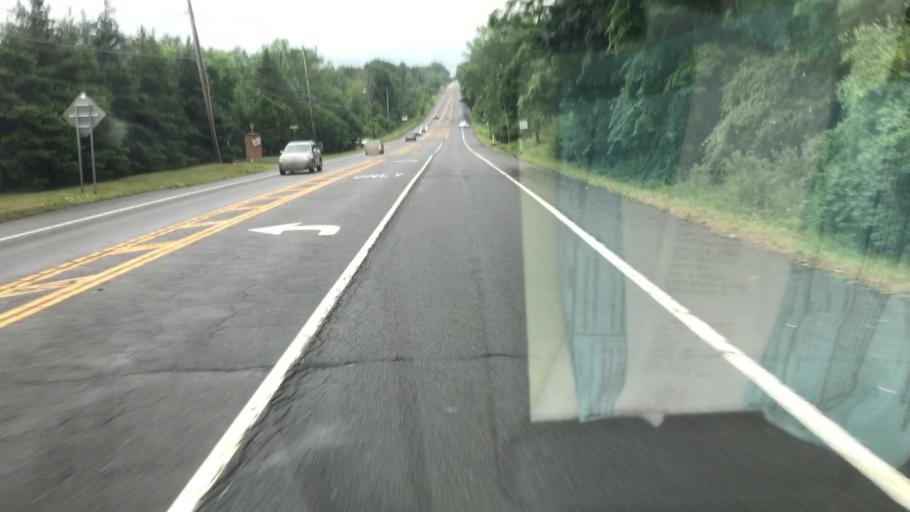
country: US
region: New York
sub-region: Onondaga County
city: Fayetteville
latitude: 43.0217
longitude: -76.0299
